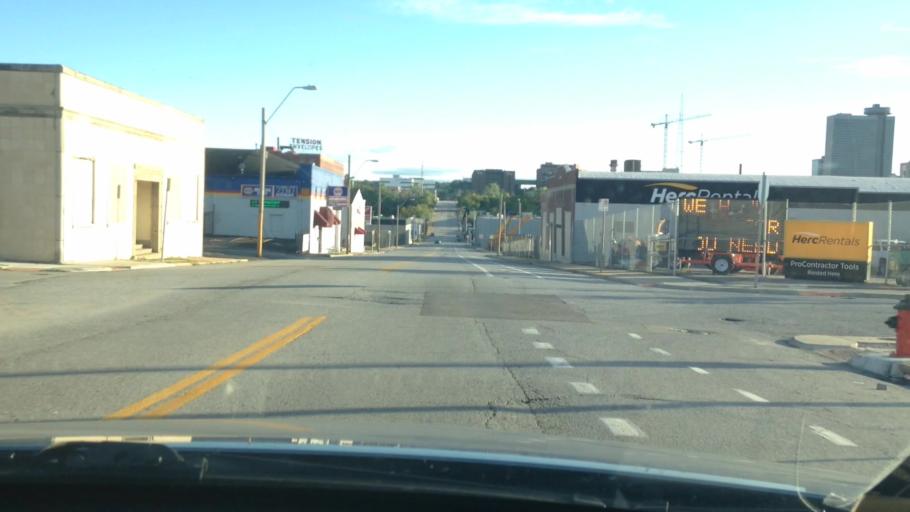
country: US
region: Missouri
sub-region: Jackson County
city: Kansas City
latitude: 39.0944
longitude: -94.5743
